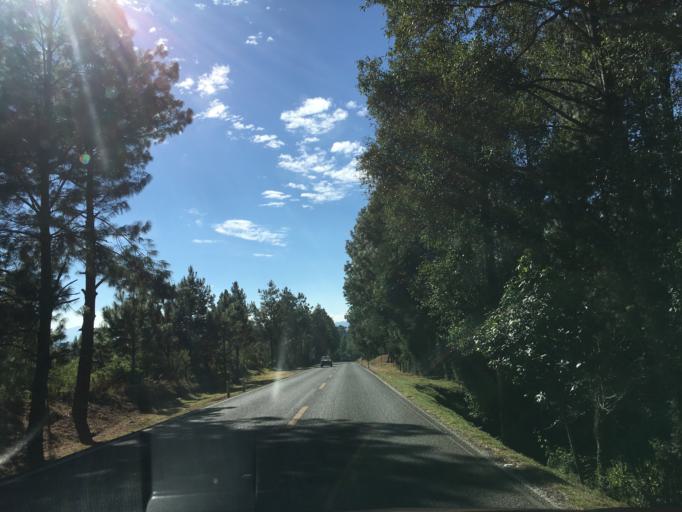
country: MX
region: Michoacan
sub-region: Hidalgo
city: Tierras Coloradas (San Pedro)
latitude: 19.7276
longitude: -100.7568
